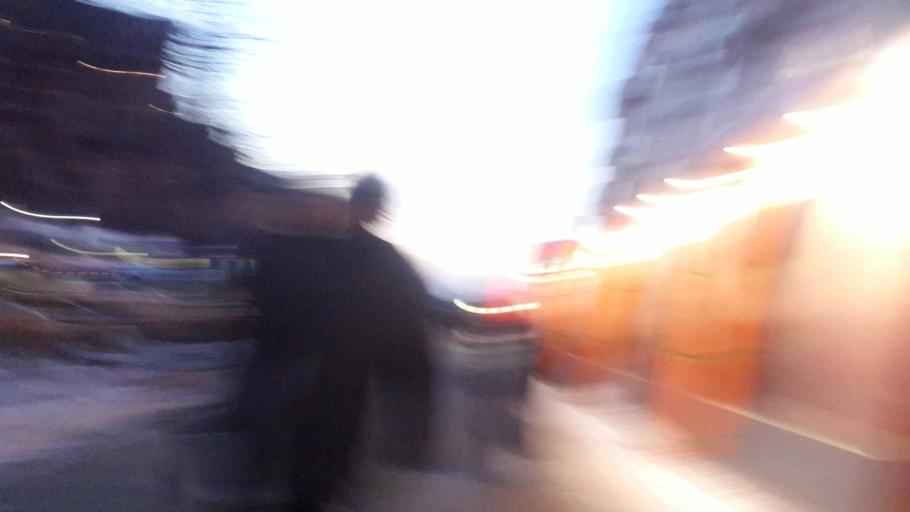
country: RU
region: Tula
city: Tula
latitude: 54.1968
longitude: 37.6056
